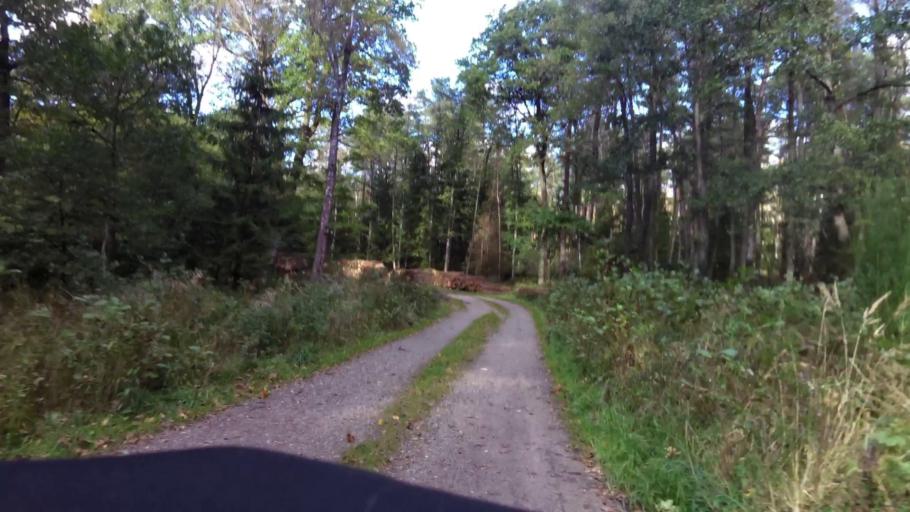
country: PL
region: West Pomeranian Voivodeship
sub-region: Powiat bialogardzki
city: Bialogard
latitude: 54.0425
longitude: 16.1355
